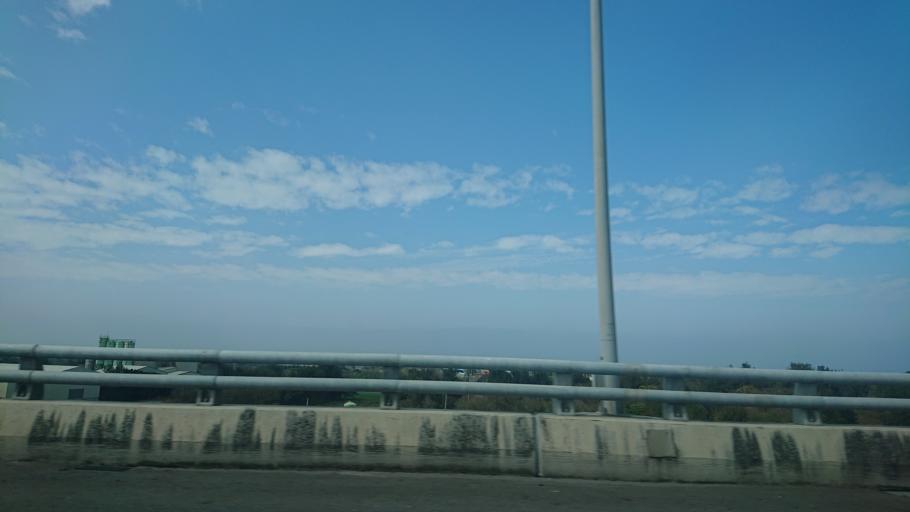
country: TW
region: Taiwan
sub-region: Yunlin
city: Douliu
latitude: 23.8551
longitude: 120.2962
